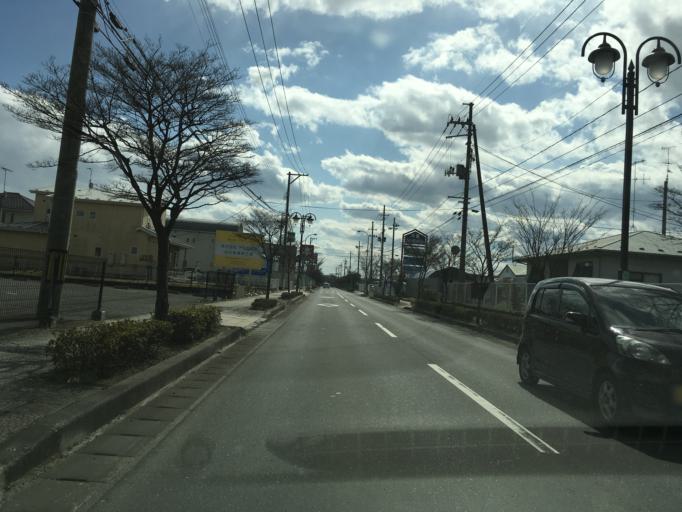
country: JP
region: Miyagi
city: Wakuya
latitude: 38.7006
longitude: 141.2112
